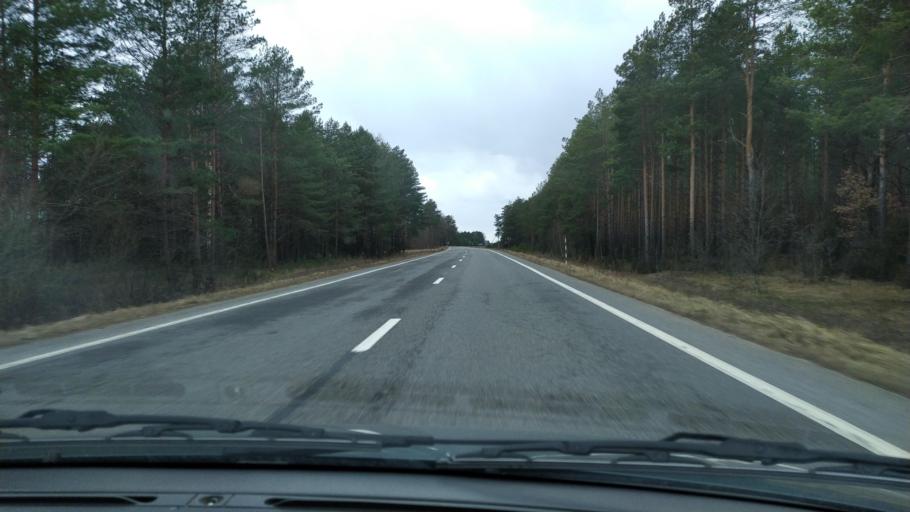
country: BY
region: Brest
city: Zhabinka
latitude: 52.3994
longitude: 24.0146
